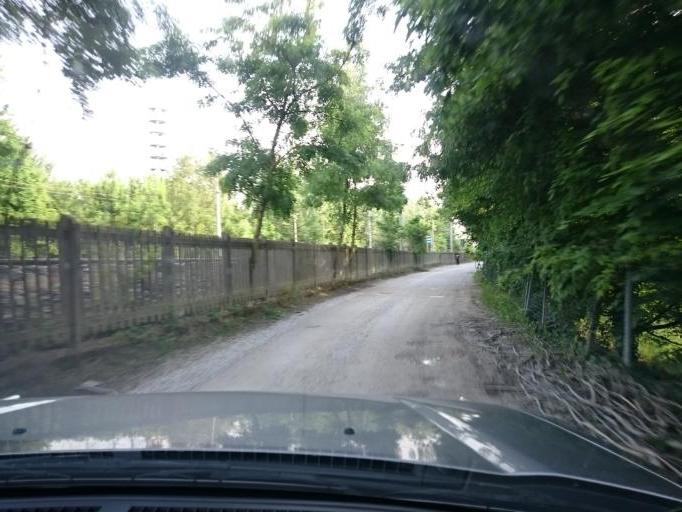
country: IT
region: Veneto
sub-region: Provincia di Padova
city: Noventa
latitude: 45.4006
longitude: 11.9237
